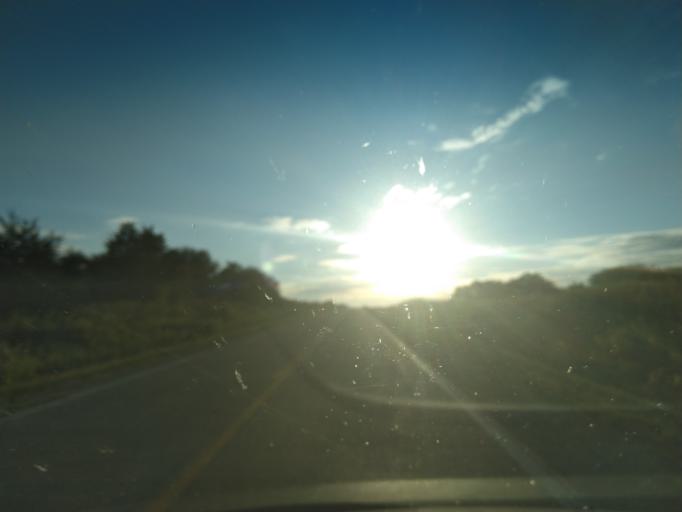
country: US
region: Iowa
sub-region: Jackson County
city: Maquoketa
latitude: 42.1644
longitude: -90.6914
